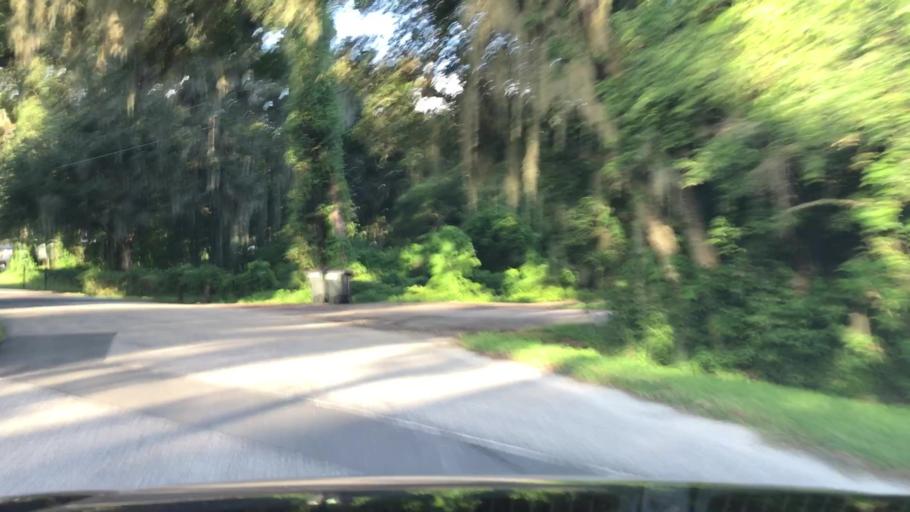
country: US
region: Florida
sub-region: Sarasota County
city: Fruitville
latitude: 27.3330
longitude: -82.4082
